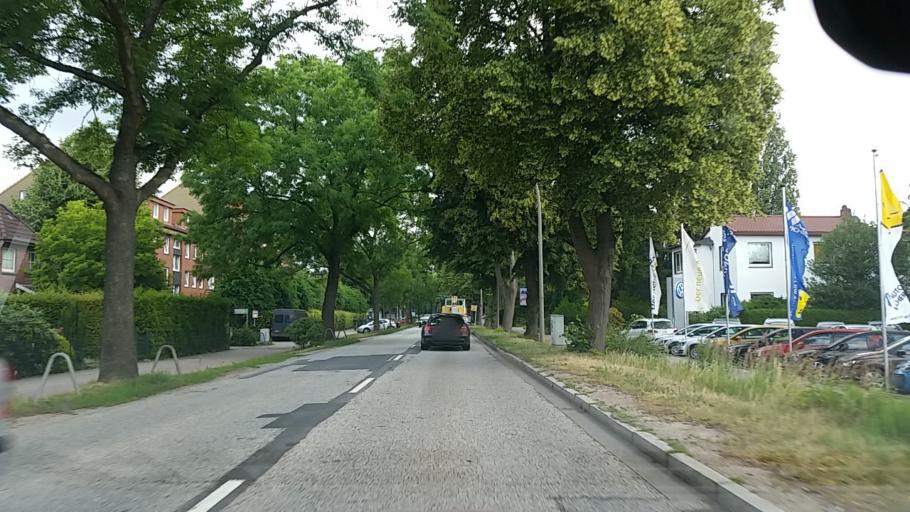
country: DE
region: Hamburg
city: Eidelstedt
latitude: 53.6255
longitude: 9.9094
